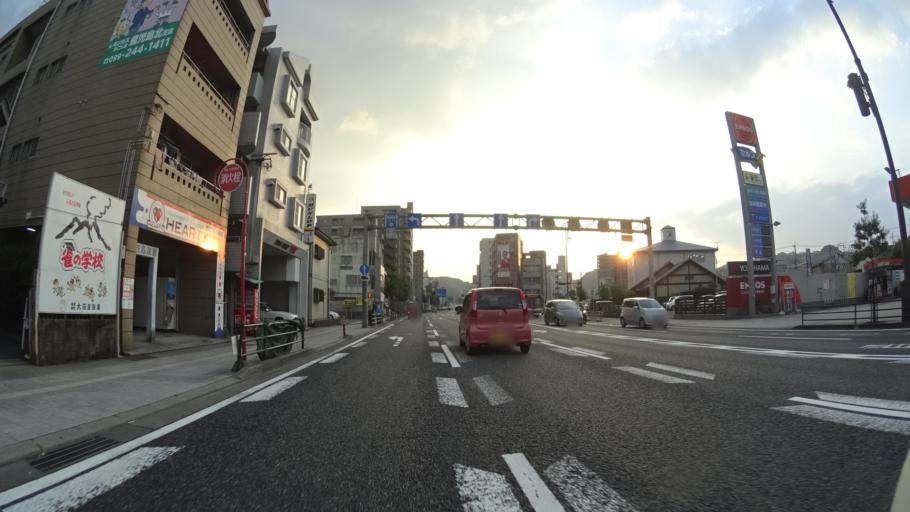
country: JP
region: Kagoshima
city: Kagoshima-shi
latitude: 31.6045
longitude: 130.5648
